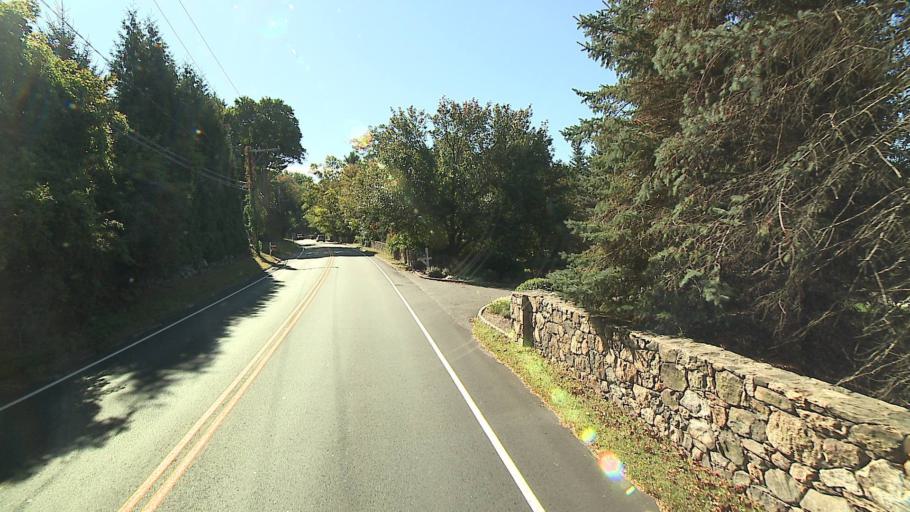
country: US
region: Connecticut
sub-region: Fairfield County
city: Darien
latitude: 41.1072
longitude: -73.4849
